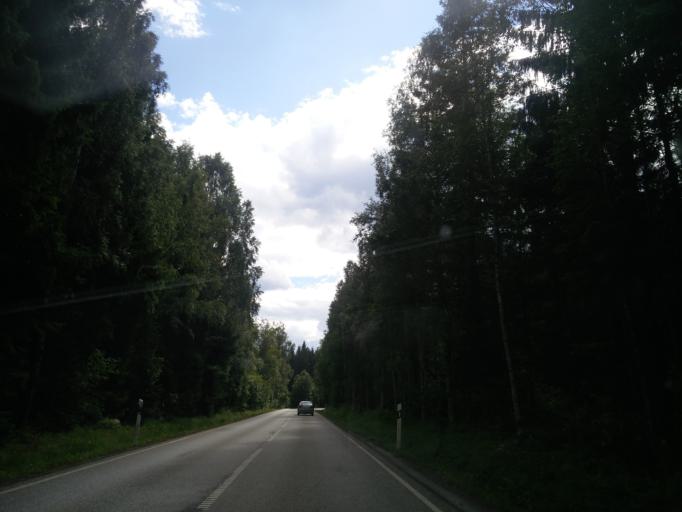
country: SE
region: OErebro
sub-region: Ljusnarsbergs Kommun
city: Kopparberg
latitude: 59.8578
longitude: 15.0008
